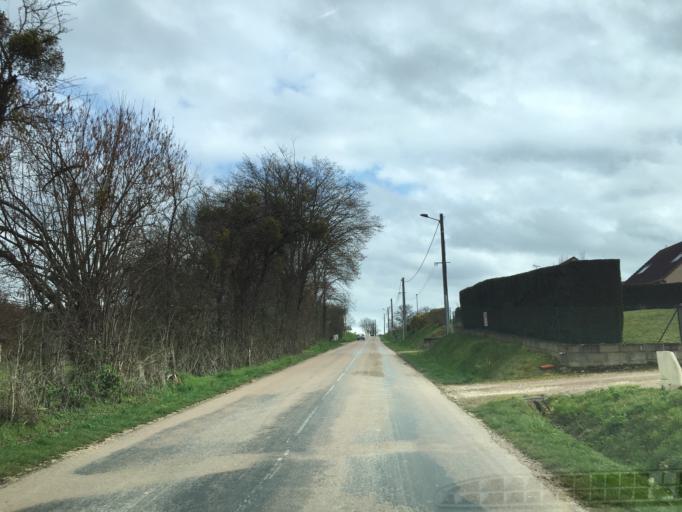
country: FR
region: Bourgogne
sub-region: Departement de l'Yonne
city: Pourrain
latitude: 47.7942
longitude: 3.3853
